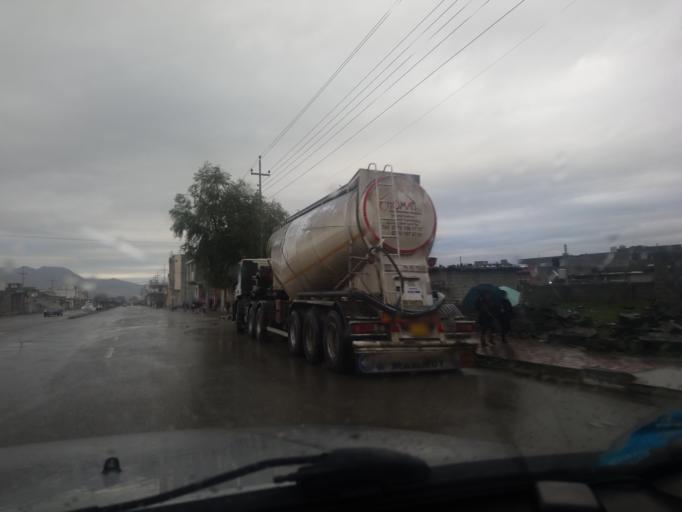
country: IQ
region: As Sulaymaniyah
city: Qeladize
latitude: 36.1776
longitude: 45.1501
